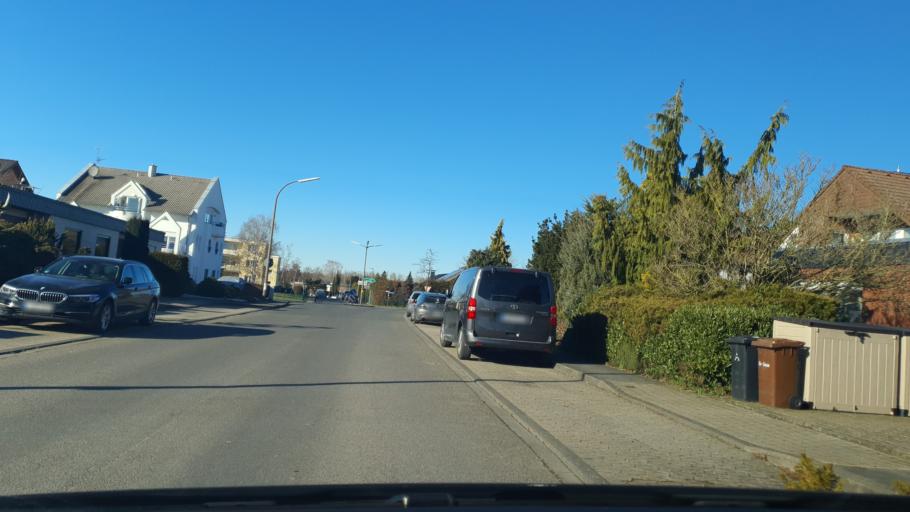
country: DE
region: North Rhine-Westphalia
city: Bornheim
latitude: 50.7205
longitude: 6.9183
